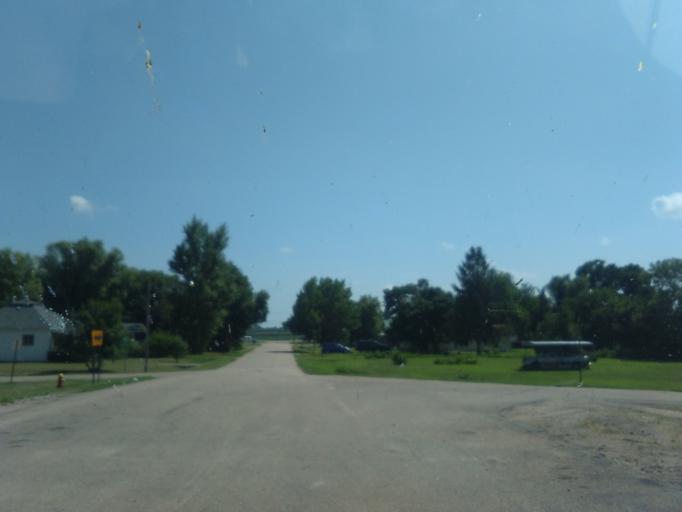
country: US
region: Nebraska
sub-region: Phelps County
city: Holdrege
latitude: 40.7168
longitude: -99.3734
